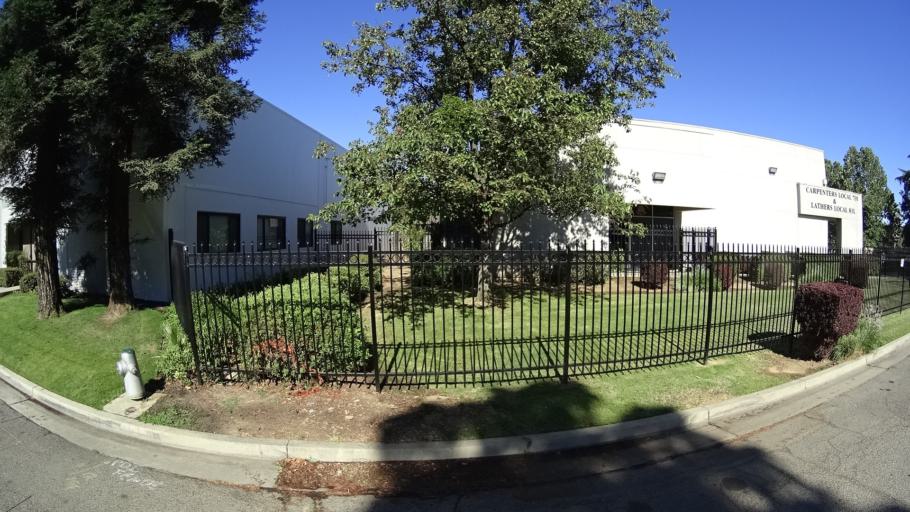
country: US
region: California
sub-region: Fresno County
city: West Park
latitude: 36.7602
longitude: -119.8338
